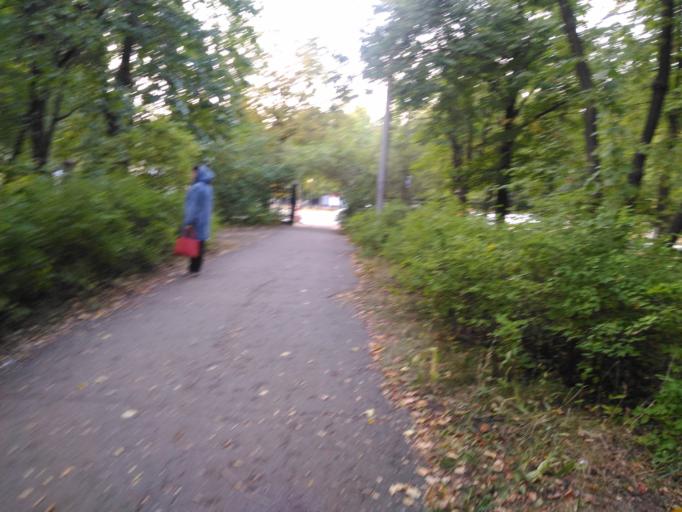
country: RU
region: Ulyanovsk
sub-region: Ulyanovskiy Rayon
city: Ulyanovsk
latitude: 54.3042
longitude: 48.3240
